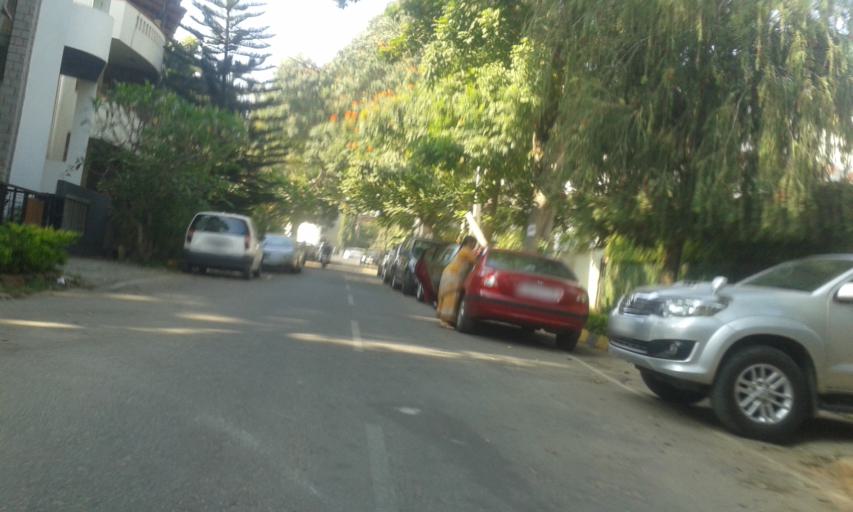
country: IN
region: Karnataka
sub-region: Bangalore Urban
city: Bangalore
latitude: 12.9355
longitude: 77.6258
